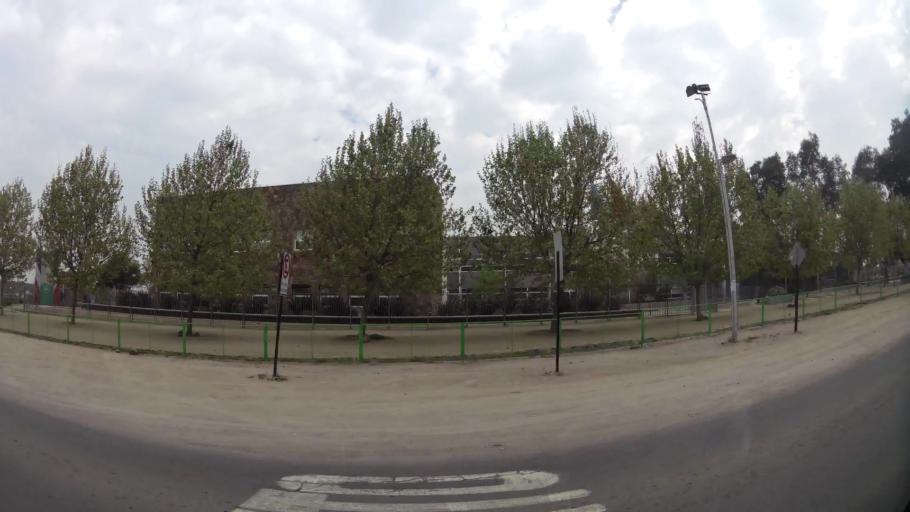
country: CL
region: Santiago Metropolitan
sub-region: Provincia de Chacabuco
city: Chicureo Abajo
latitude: -33.2052
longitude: -70.6834
